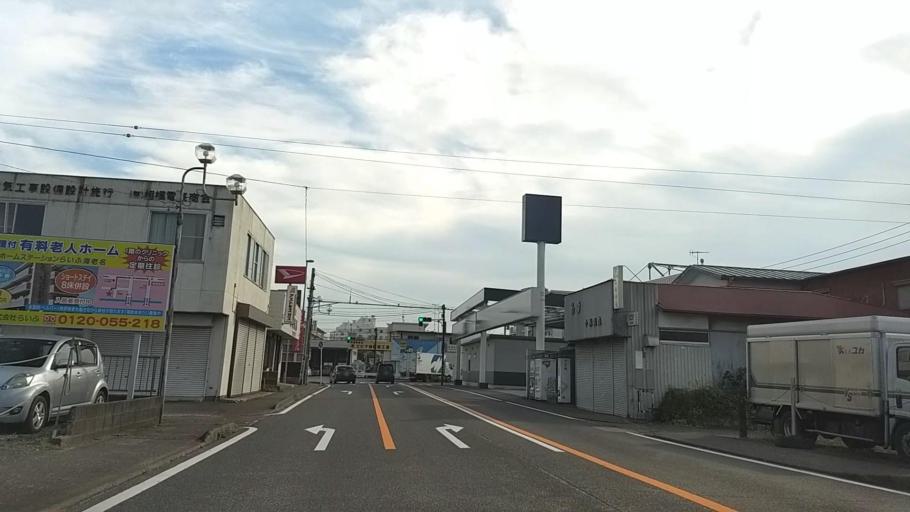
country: JP
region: Kanagawa
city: Atsugi
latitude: 35.4447
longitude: 139.3766
